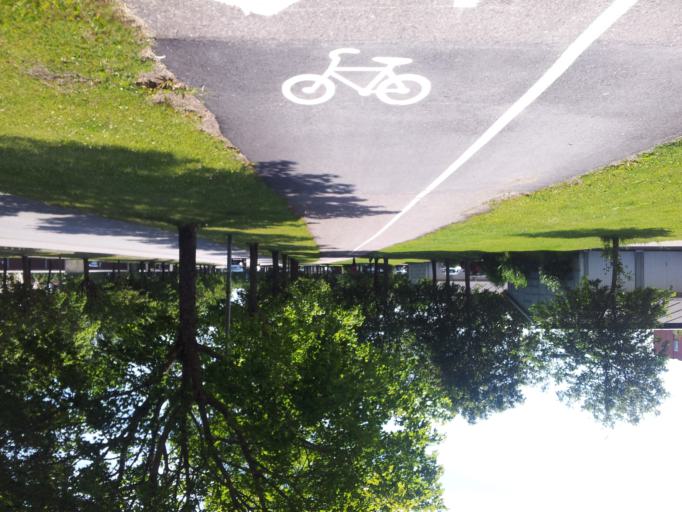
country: SE
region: Uppsala
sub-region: Uppsala Kommun
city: Uppsala
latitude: 59.8782
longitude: 17.6561
